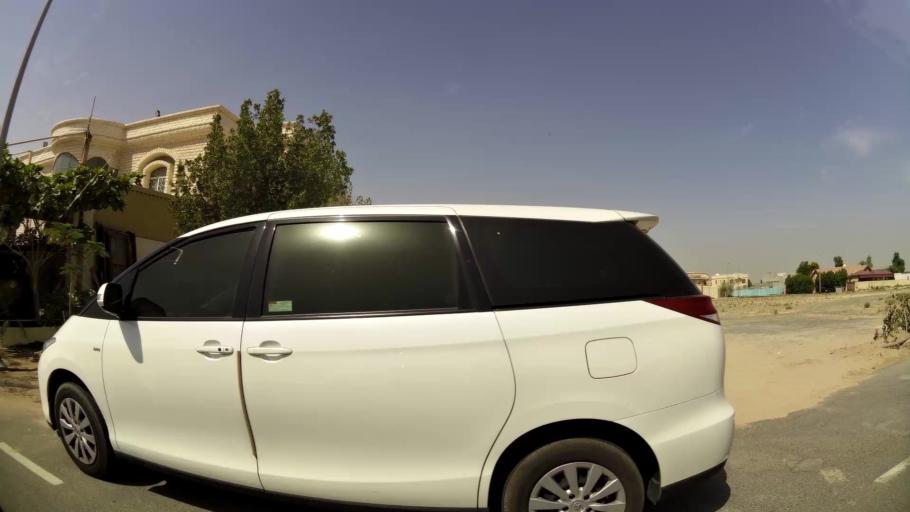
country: AE
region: Ash Shariqah
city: Sharjah
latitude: 25.1970
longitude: 55.4395
